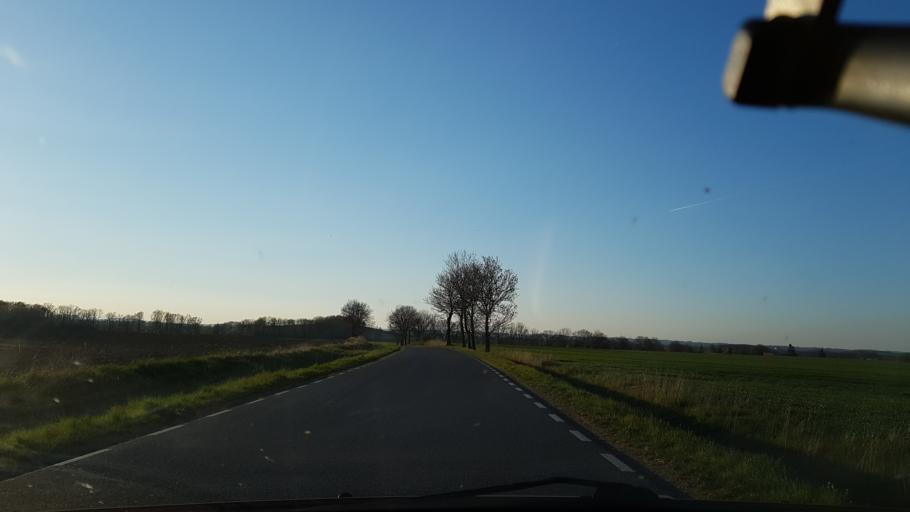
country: CZ
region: Olomoucky
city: Vidnava
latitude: 50.4168
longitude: 17.1827
